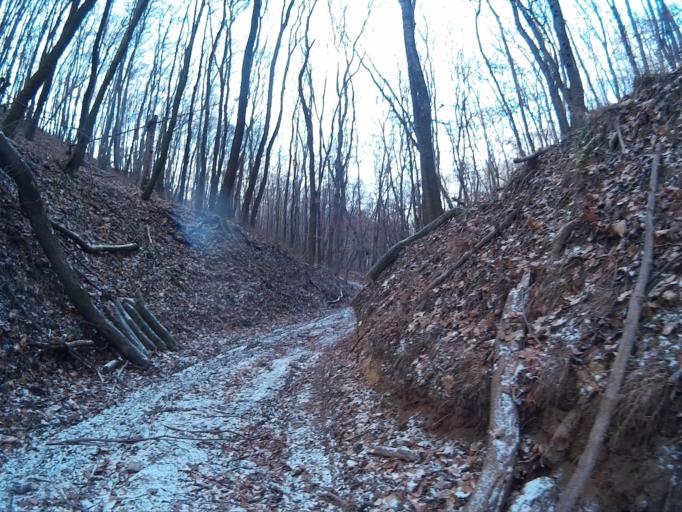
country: HU
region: Komarom-Esztergom
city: Tatabanya
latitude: 47.5141
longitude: 18.4193
